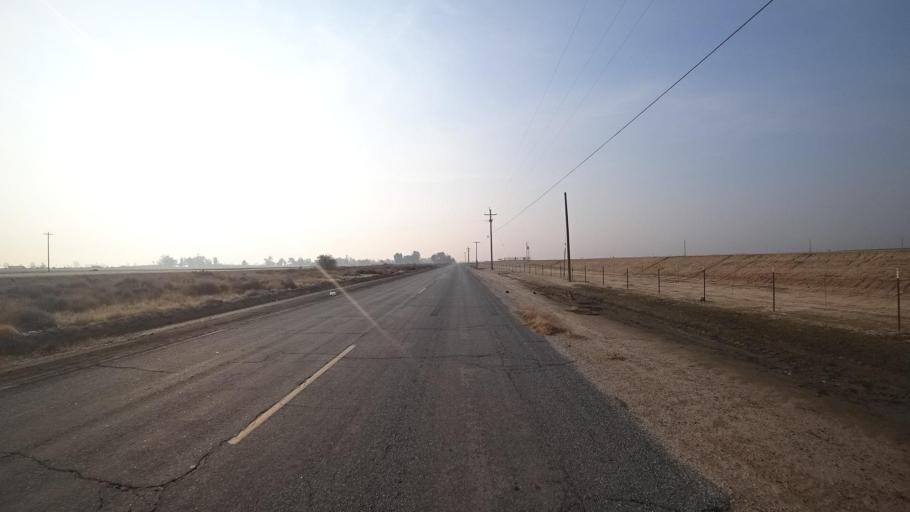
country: US
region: California
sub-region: Kern County
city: Greenfield
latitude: 35.2436
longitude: -119.0214
